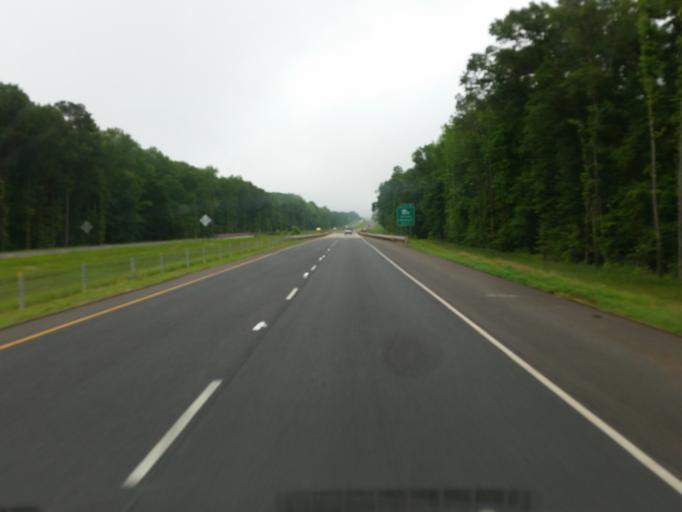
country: US
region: Louisiana
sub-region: Bienville Parish
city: Arcadia
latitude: 32.5632
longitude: -93.0922
